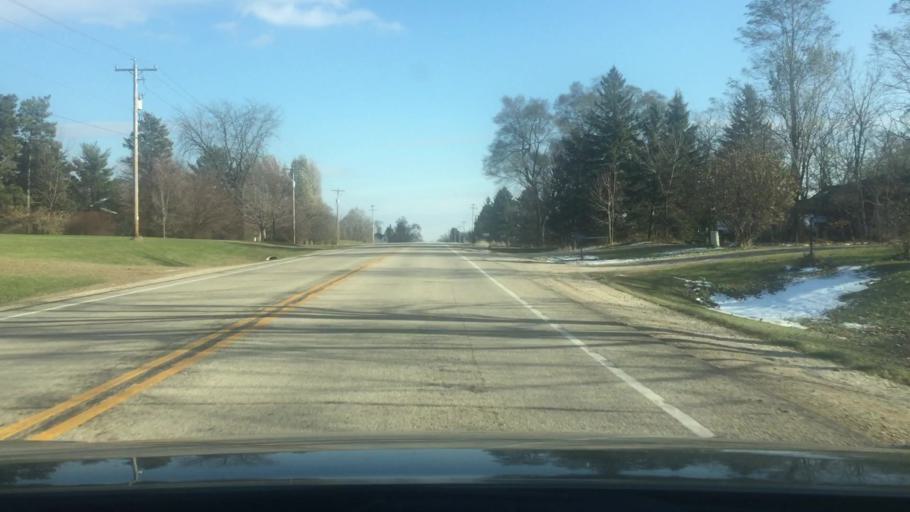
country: US
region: Wisconsin
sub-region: Jefferson County
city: Jefferson
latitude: 42.9375
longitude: -88.7372
